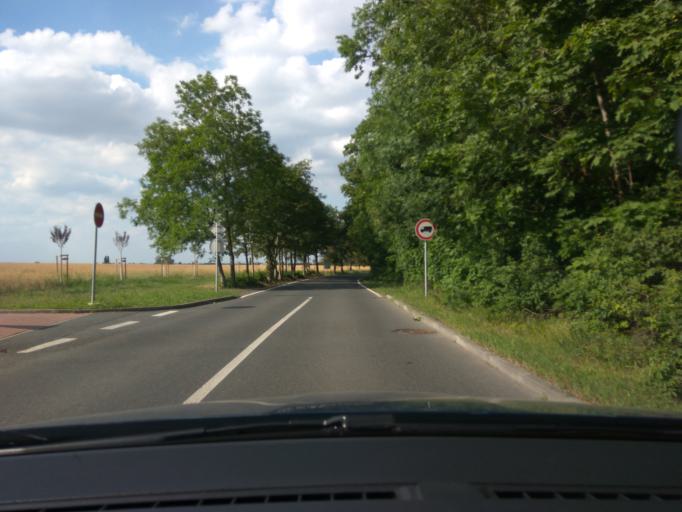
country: CZ
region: Praha
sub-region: Praha 19
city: Satalice
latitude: 50.1297
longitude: 14.5730
